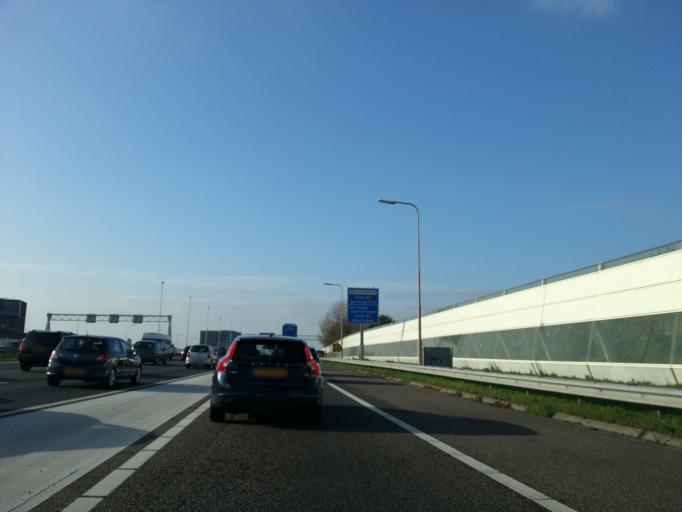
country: NL
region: South Holland
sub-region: Gemeente Den Haag
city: Ypenburg
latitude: 52.0548
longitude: 4.3984
